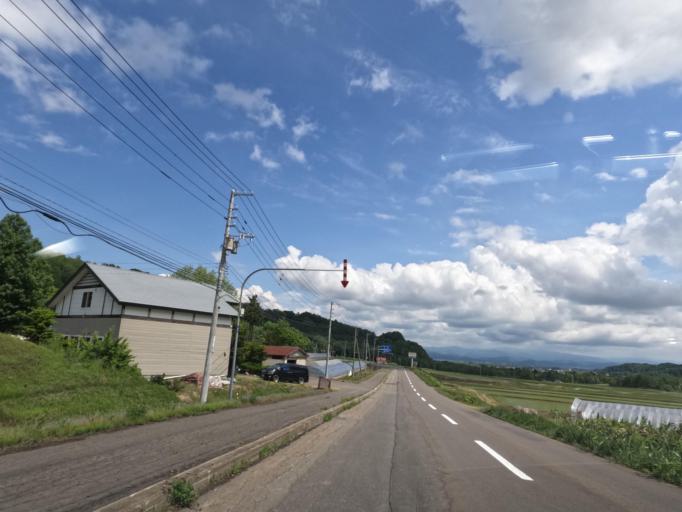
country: JP
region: Hokkaido
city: Takikawa
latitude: 43.5802
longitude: 141.8253
